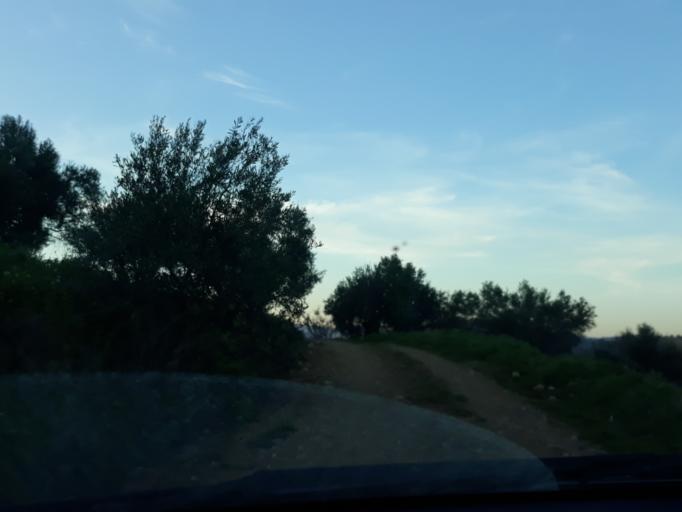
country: GR
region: Central Greece
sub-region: Nomos Voiotias
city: Asopia
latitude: 38.2782
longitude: 23.5303
